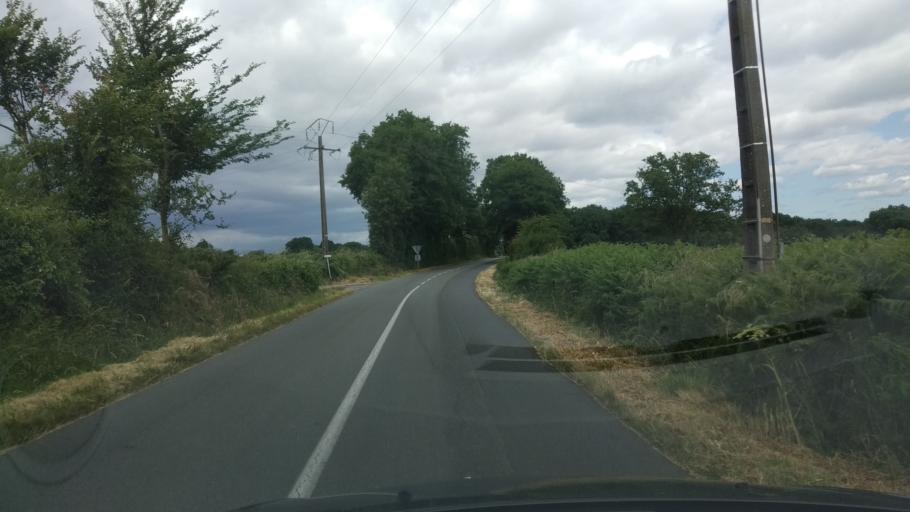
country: FR
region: Poitou-Charentes
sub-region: Departement de la Vienne
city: Vouneuil-sous-Biard
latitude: 46.5598
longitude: 0.2631
